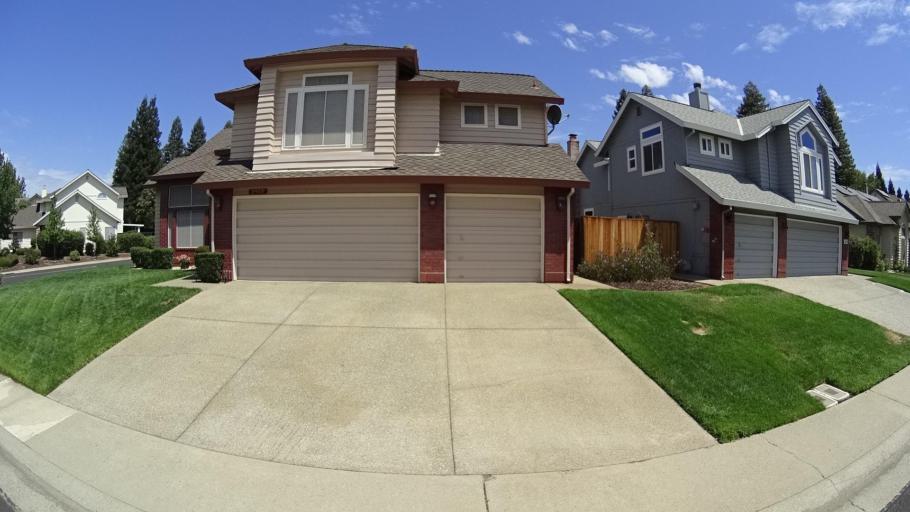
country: US
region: California
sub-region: Placer County
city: Rocklin
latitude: 38.8080
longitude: -121.2539
